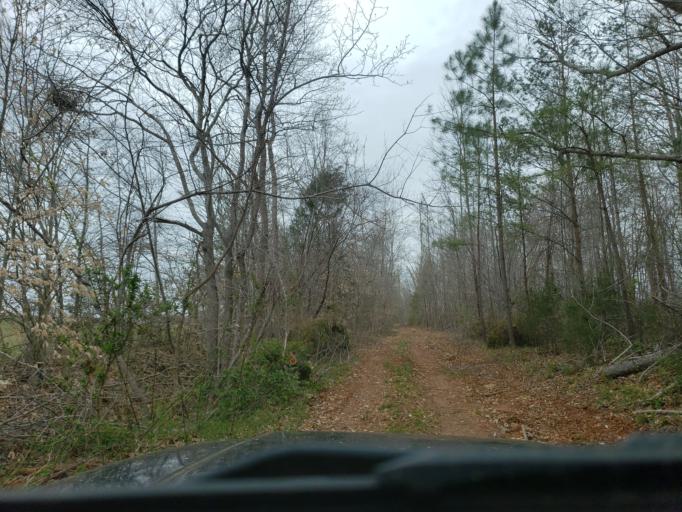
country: US
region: North Carolina
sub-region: Cleveland County
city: White Plains
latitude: 35.1887
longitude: -81.3700
